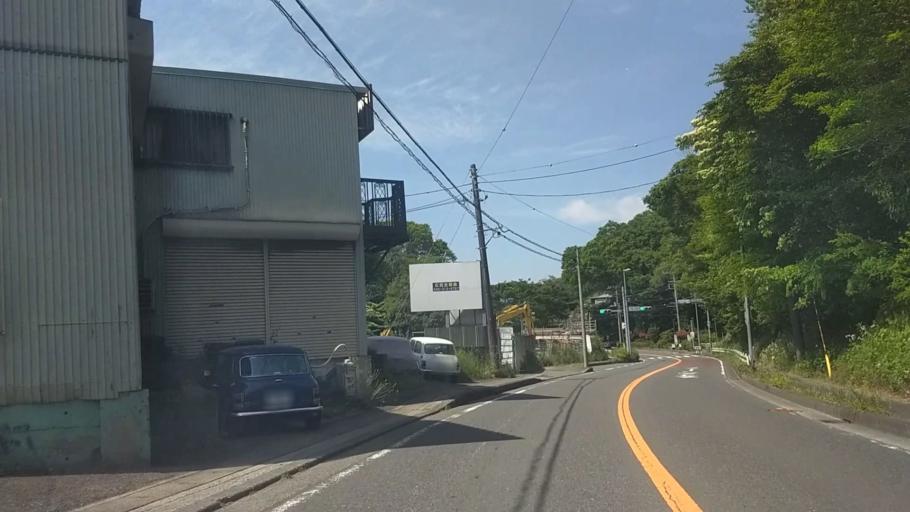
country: JP
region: Kanagawa
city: Kamakura
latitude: 35.3435
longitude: 139.5820
